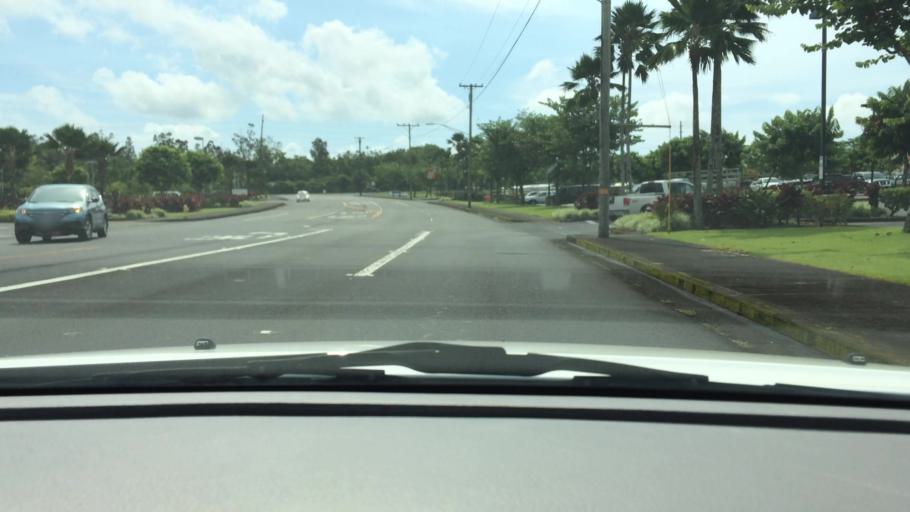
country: US
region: Hawaii
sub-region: Hawaii County
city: Hilo
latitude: 19.6992
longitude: -155.0604
